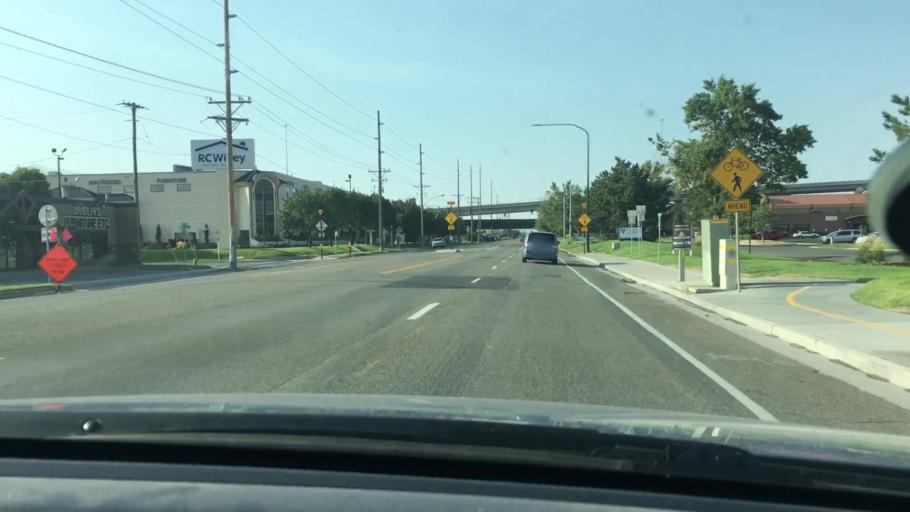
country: US
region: Utah
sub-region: Salt Lake County
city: South Salt Lake
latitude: 40.7220
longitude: -111.8998
